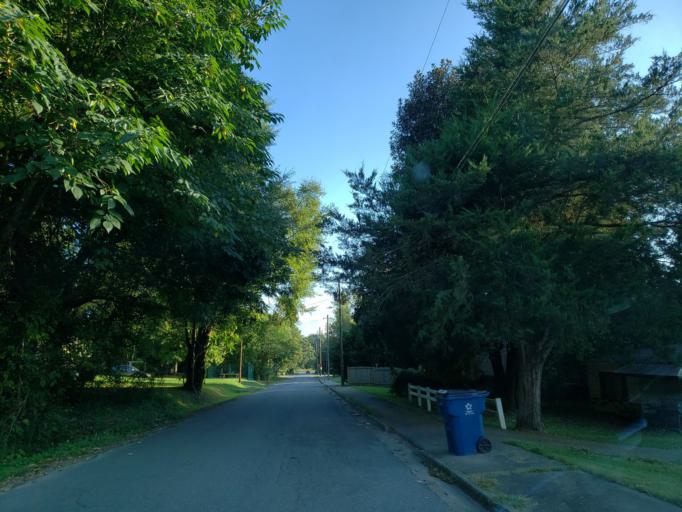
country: US
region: Georgia
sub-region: Bartow County
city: Euharlee
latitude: 34.2397
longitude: -84.9450
